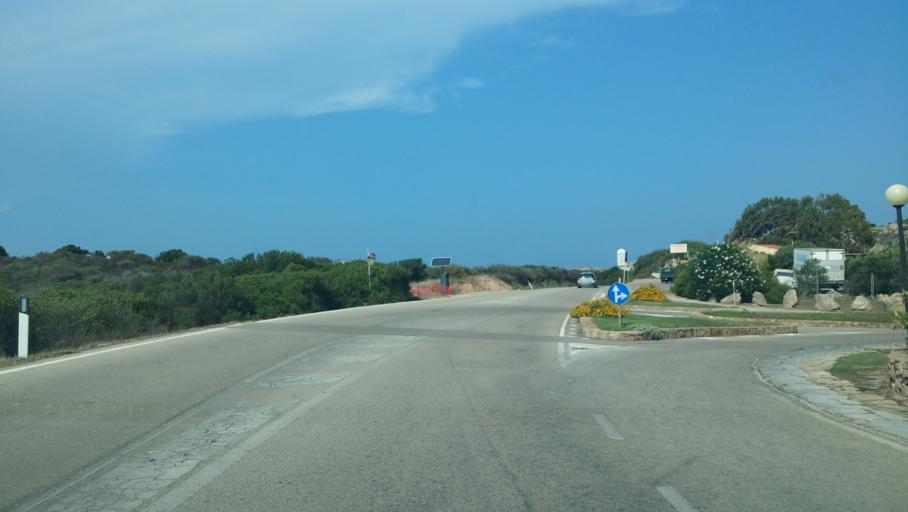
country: IT
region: Sardinia
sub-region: Provincia di Olbia-Tempio
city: La Maddalena
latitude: 41.2400
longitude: 9.4271
